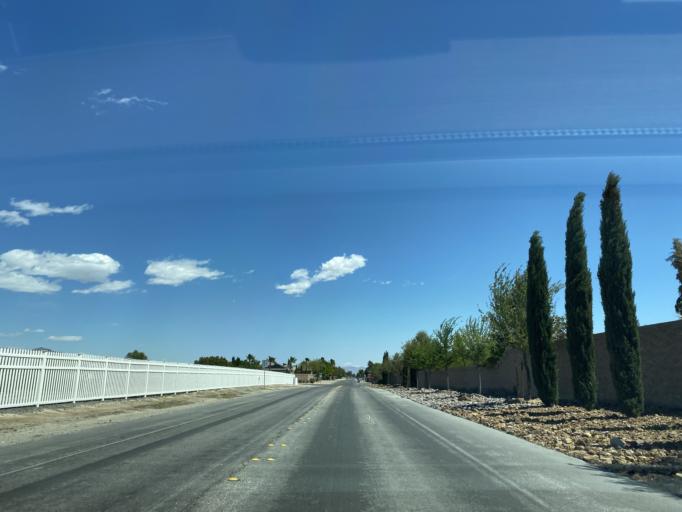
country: US
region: Nevada
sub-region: Clark County
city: North Las Vegas
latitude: 36.3015
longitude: -115.2440
